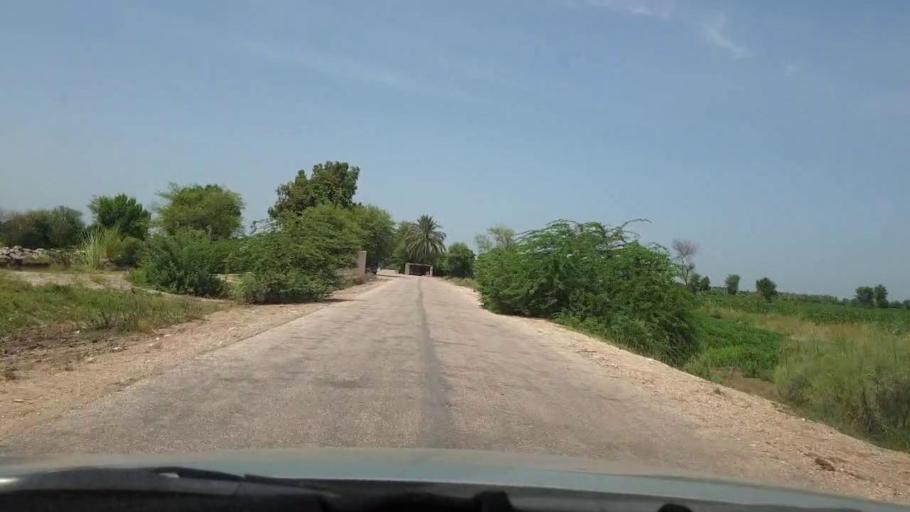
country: PK
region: Sindh
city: Pano Aqil
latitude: 27.6682
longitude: 69.1084
